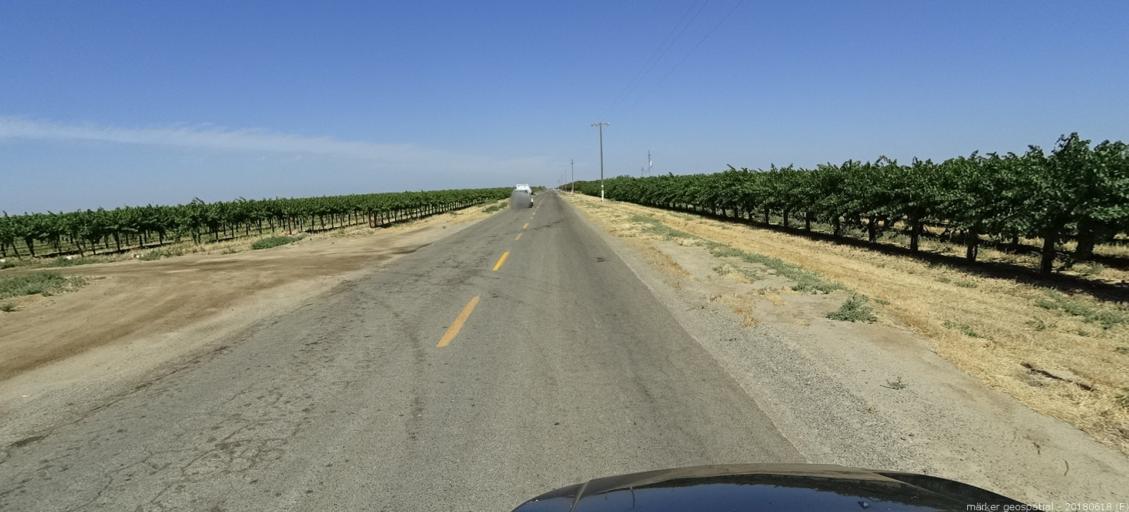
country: US
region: California
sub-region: Fresno County
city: Mendota
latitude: 36.8366
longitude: -120.2169
